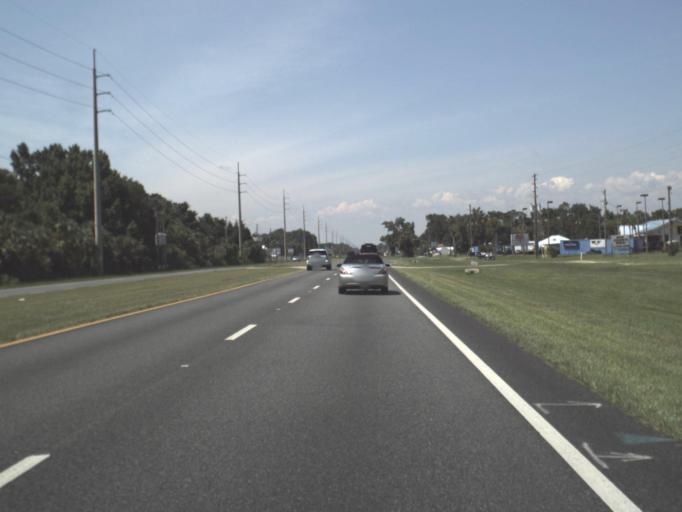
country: US
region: Florida
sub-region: Citrus County
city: Homosassa Springs
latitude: 28.8301
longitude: -82.5793
